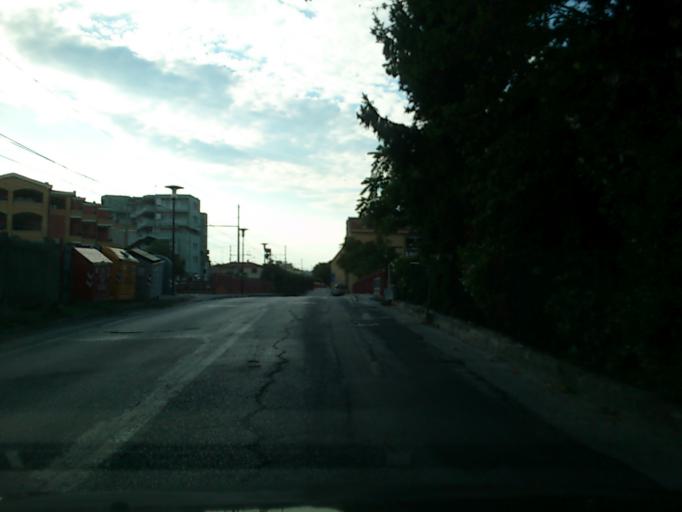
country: IT
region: The Marches
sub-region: Provincia di Pesaro e Urbino
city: Fano
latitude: 43.8480
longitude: 13.0148
